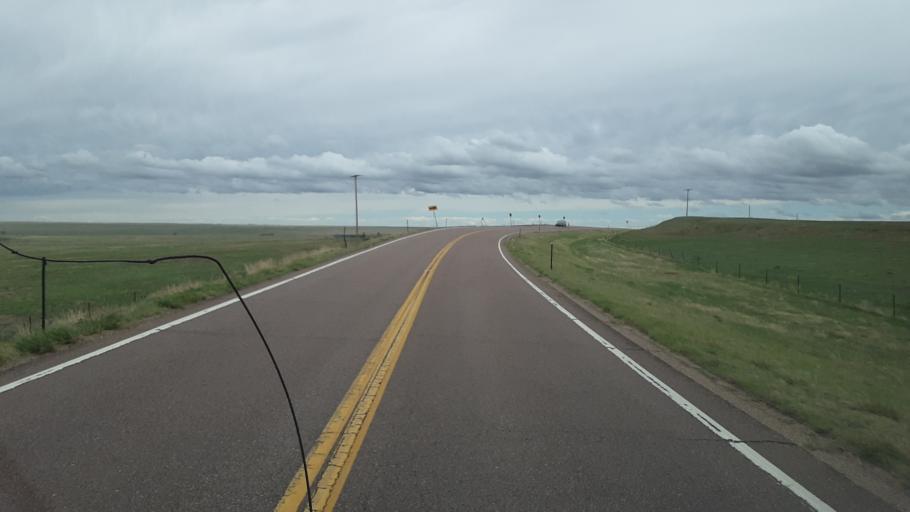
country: US
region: Colorado
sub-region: Lincoln County
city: Limon
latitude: 38.8390
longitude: -103.8104
